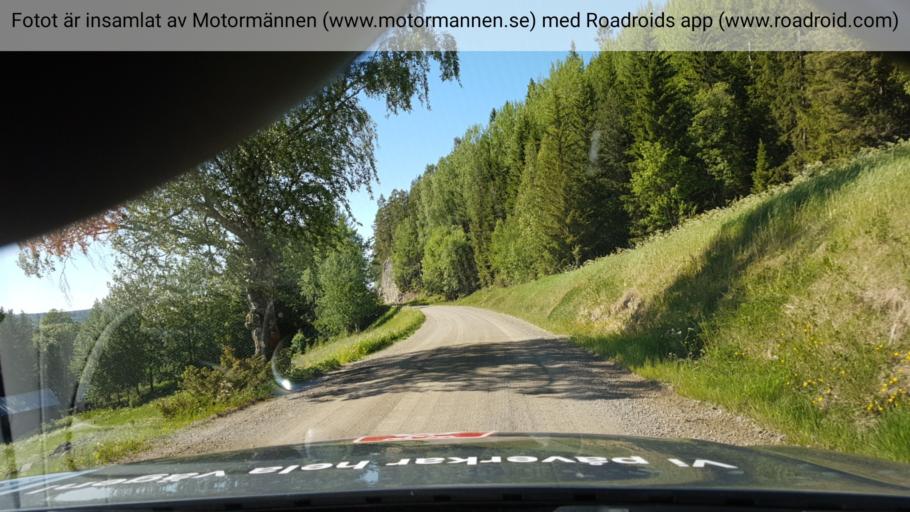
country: SE
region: Jaemtland
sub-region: OEstersunds Kommun
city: Brunflo
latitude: 62.9549
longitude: 14.9126
